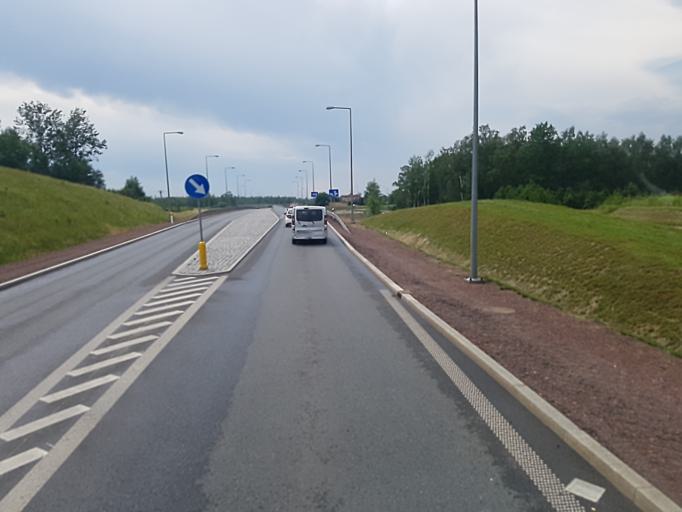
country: PL
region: Silesian Voivodeship
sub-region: Jastrzebie-Zdroj
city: Jastrzebie Zdroj
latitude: 49.9725
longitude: 18.5704
